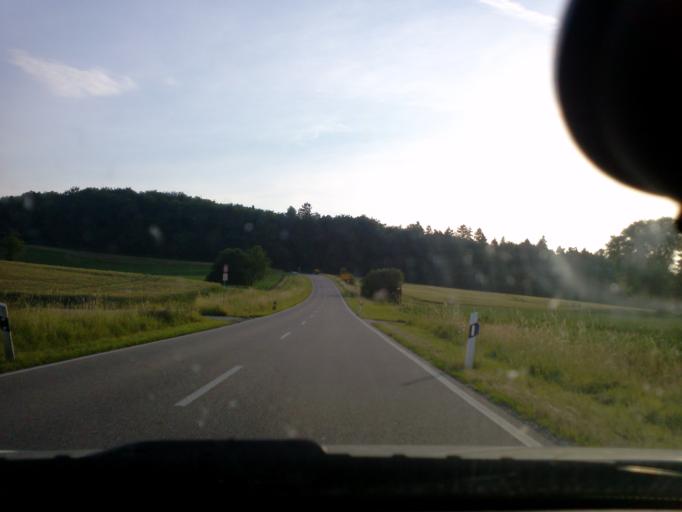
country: DE
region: Baden-Wuerttemberg
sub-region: Karlsruhe Region
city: Woessingen
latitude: 48.9888
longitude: 8.6429
